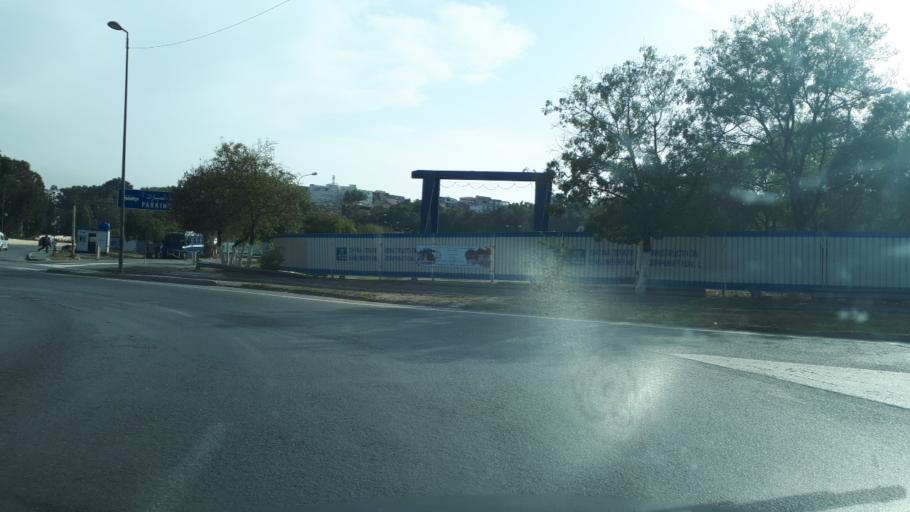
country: DZ
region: Tipaza
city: Cheraga
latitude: 36.7579
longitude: 2.9980
